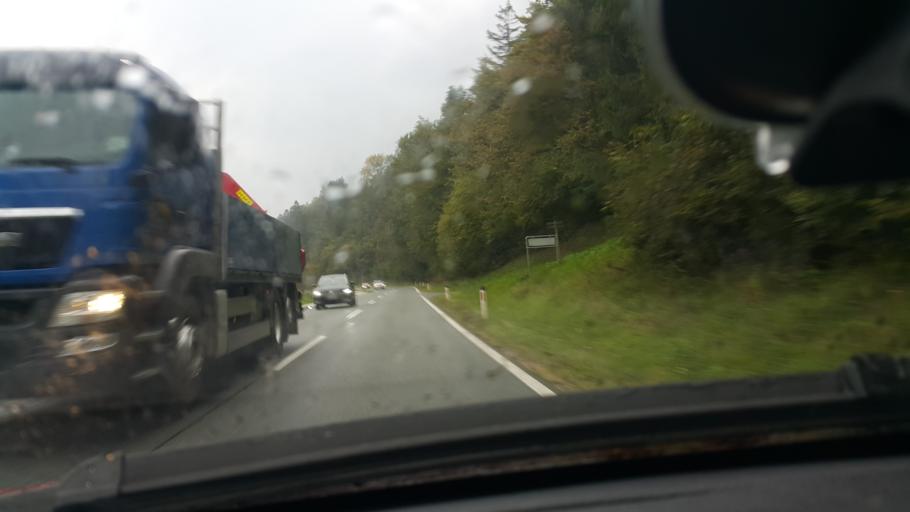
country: AT
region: Carinthia
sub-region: Politischer Bezirk Wolfsberg
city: Lavamund
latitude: 46.6175
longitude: 14.9754
